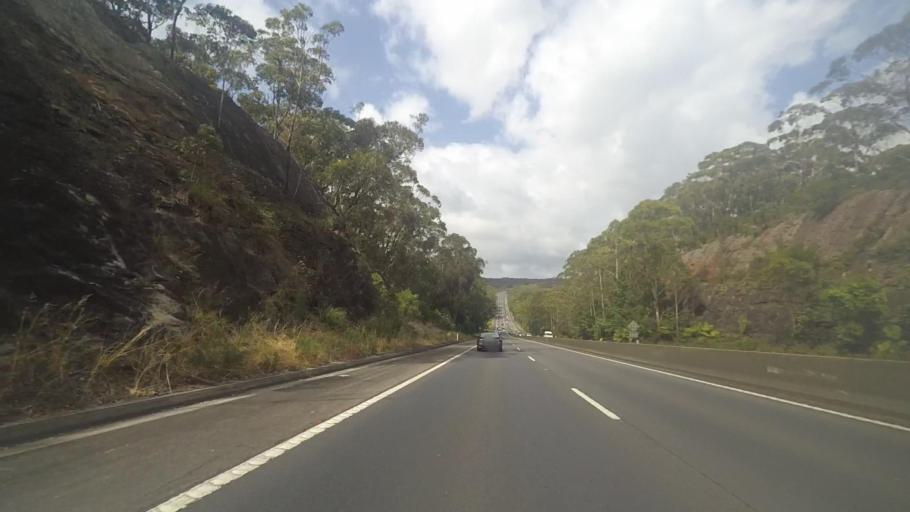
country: AU
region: New South Wales
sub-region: Wollongong
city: Bulli
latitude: -34.3473
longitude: 150.8705
